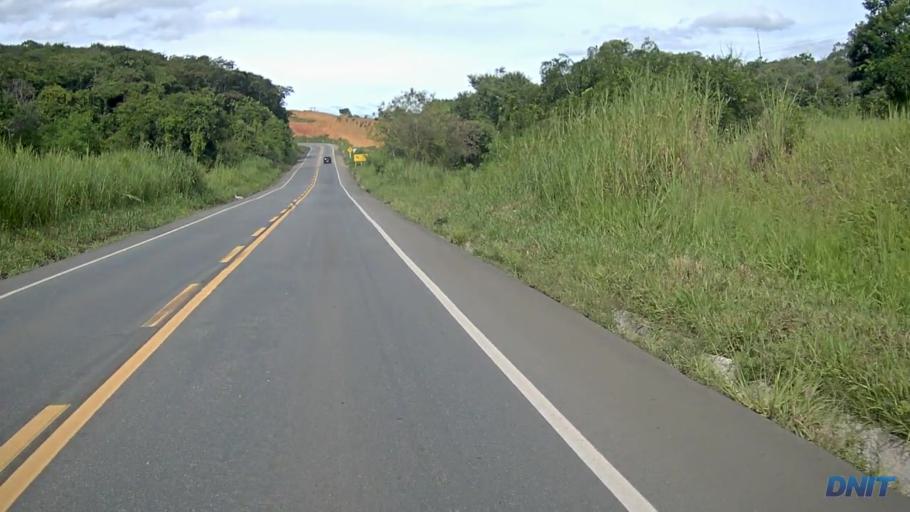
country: BR
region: Minas Gerais
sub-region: Ipaba
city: Ipaba
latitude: -19.2954
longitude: -42.3601
